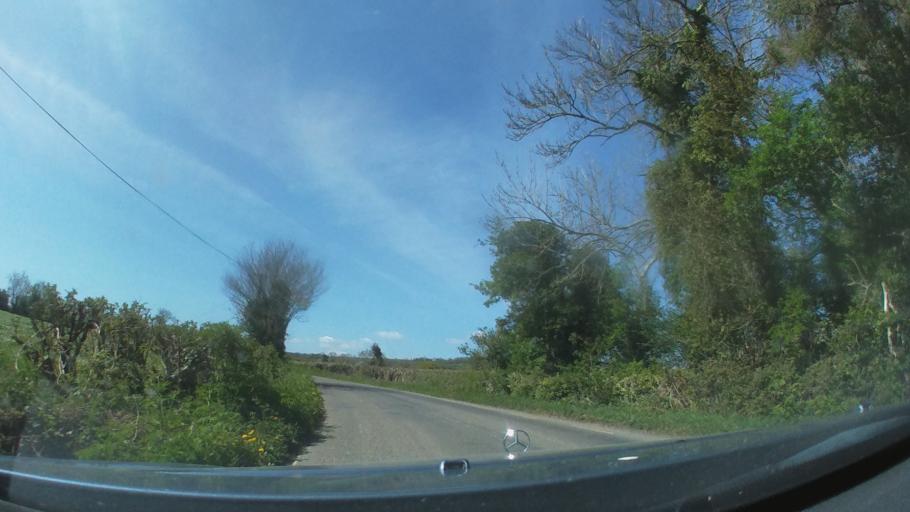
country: IE
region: Leinster
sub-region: Kilkenny
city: Callan
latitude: 52.6266
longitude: -7.3587
